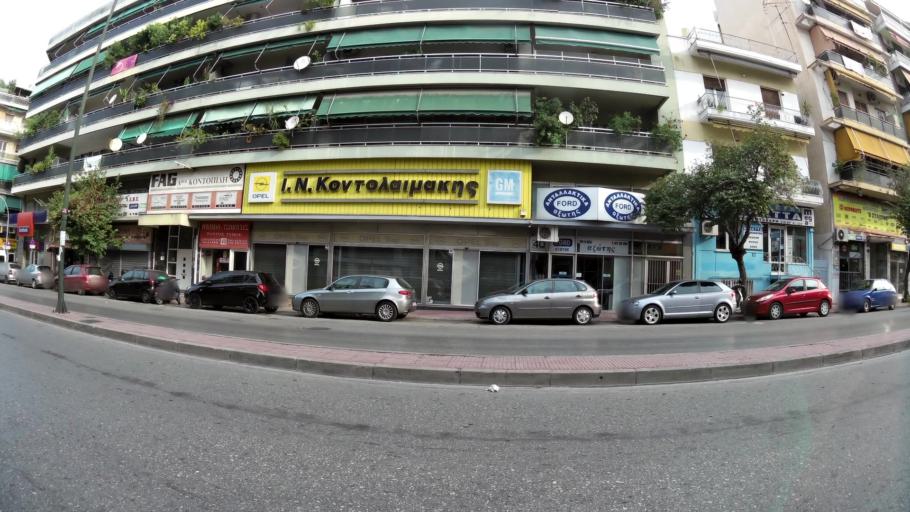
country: GR
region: Attica
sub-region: Nomarchia Athinas
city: Nea Chalkidona
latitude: 38.0131
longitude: 23.7233
